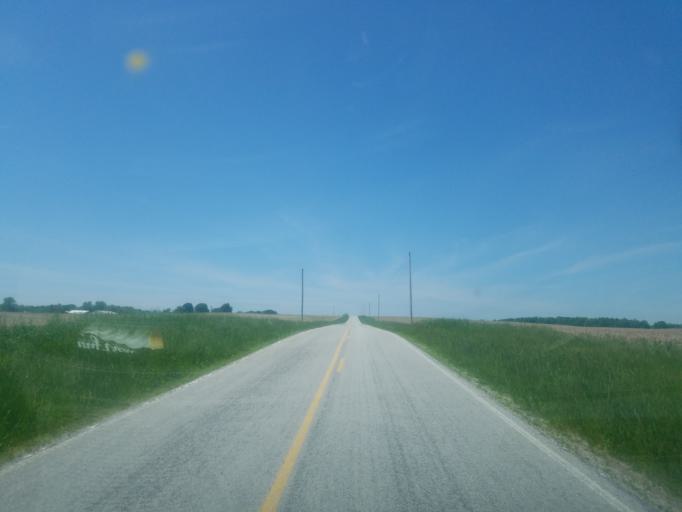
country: US
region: Ohio
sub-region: Huron County
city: New London
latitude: 41.1107
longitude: -82.4543
